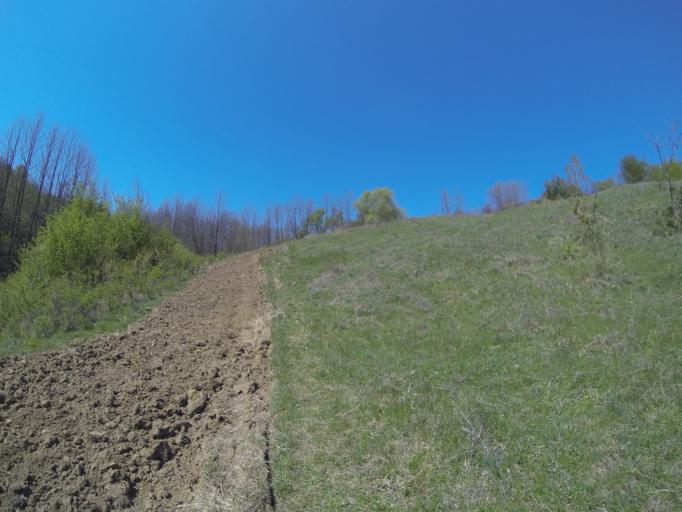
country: RO
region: Gorj
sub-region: Comuna Crusetu
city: Crusetu
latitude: 44.5862
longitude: 23.6585
